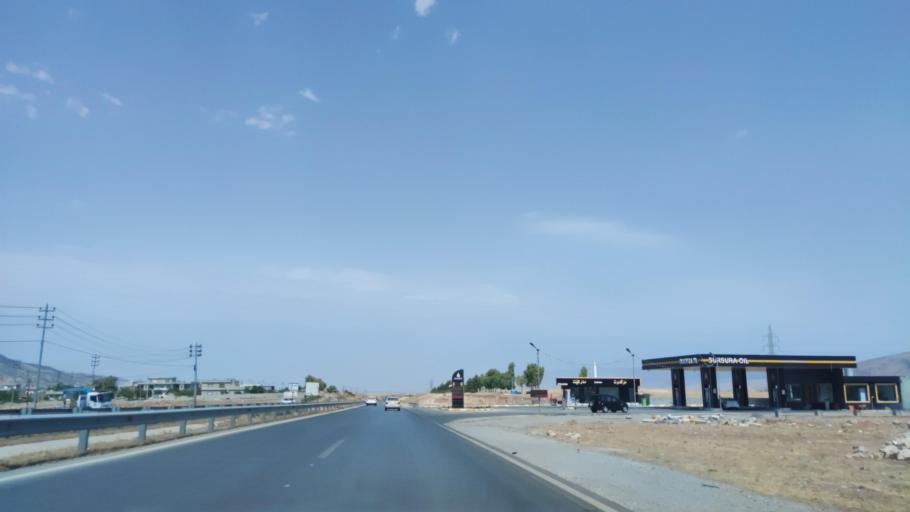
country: IQ
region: Arbil
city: Shaqlawah
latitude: 36.4986
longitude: 44.3616
